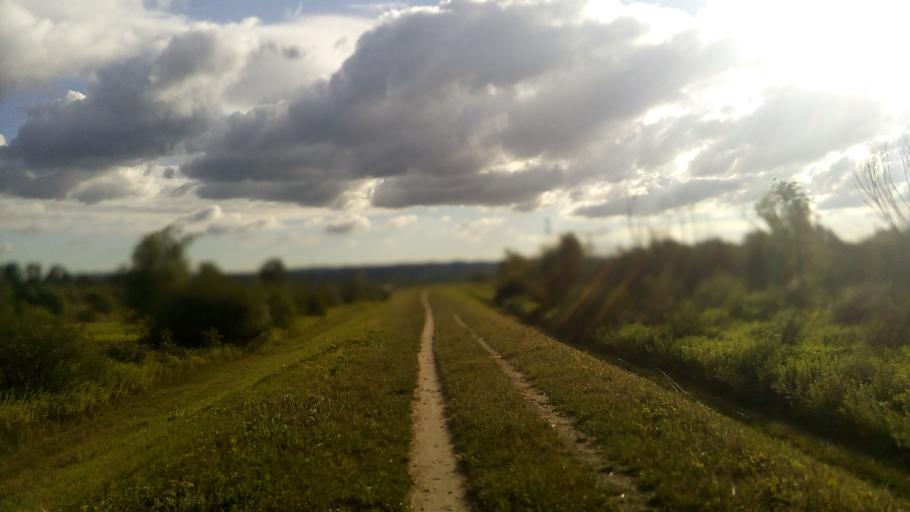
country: PL
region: Lesser Poland Voivodeship
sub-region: Powiat nowosadecki
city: Chelmiec
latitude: 49.5950
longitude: 20.6563
